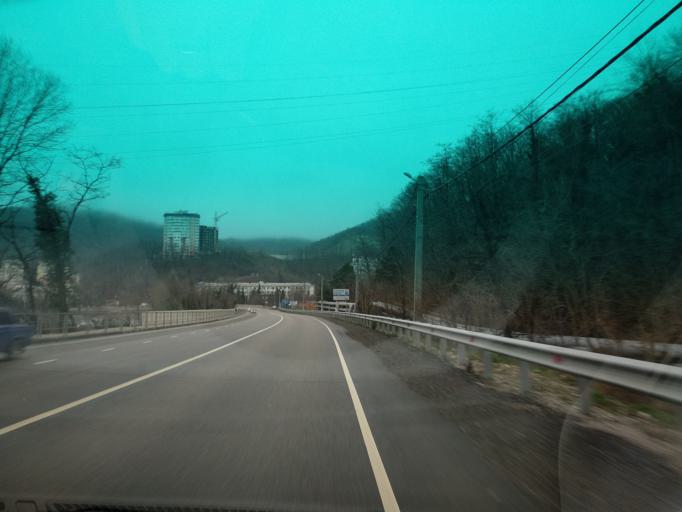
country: RU
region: Krasnodarskiy
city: Tuapse
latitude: 44.1139
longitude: 39.0699
